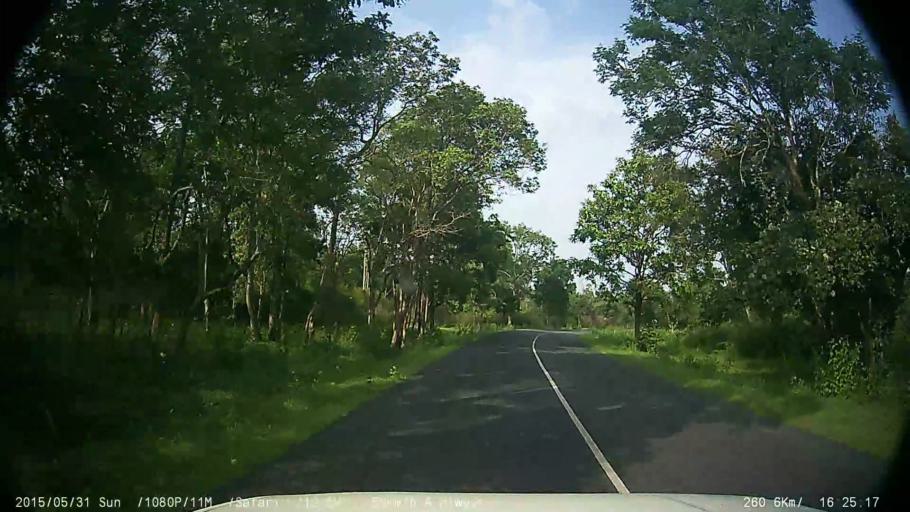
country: IN
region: Karnataka
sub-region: Chamrajnagar
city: Gundlupet
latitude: 11.7657
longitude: 76.5265
